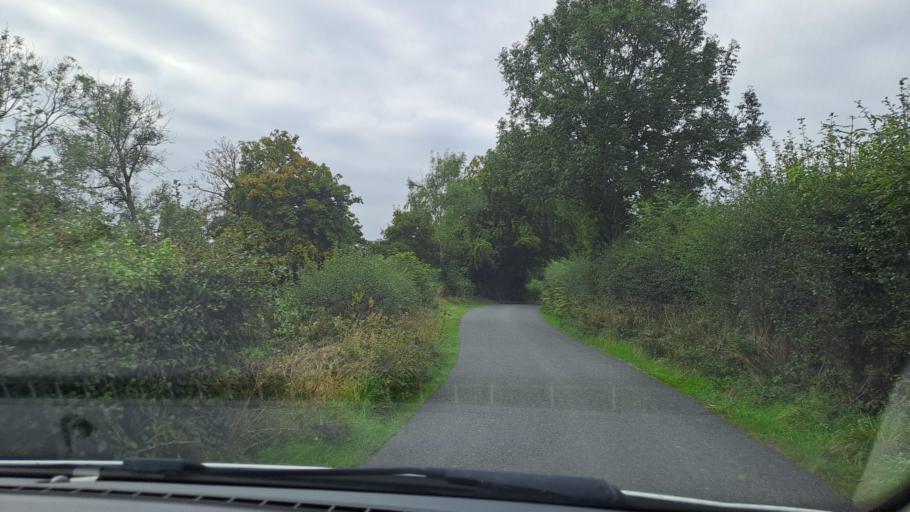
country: IE
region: Ulster
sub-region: An Cabhan
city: Kingscourt
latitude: 53.9674
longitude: -6.8542
